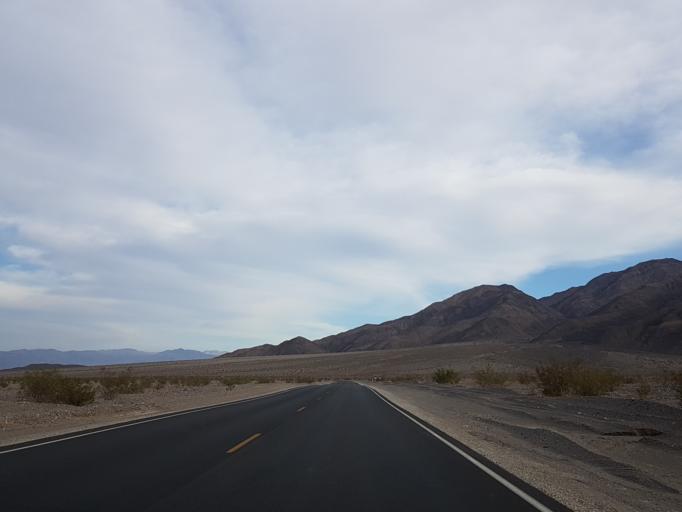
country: US
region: Nevada
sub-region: Nye County
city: Beatty
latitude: 36.6057
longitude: -117.1329
